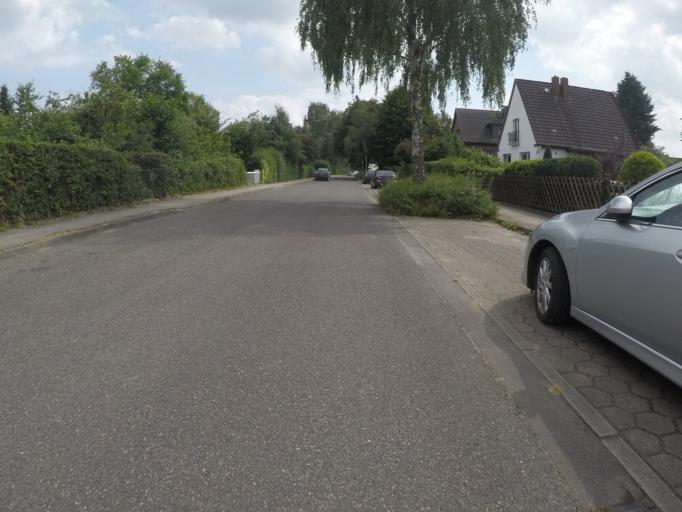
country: DE
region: Hamburg
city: Wandsbek
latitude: 53.5487
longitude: 10.1168
